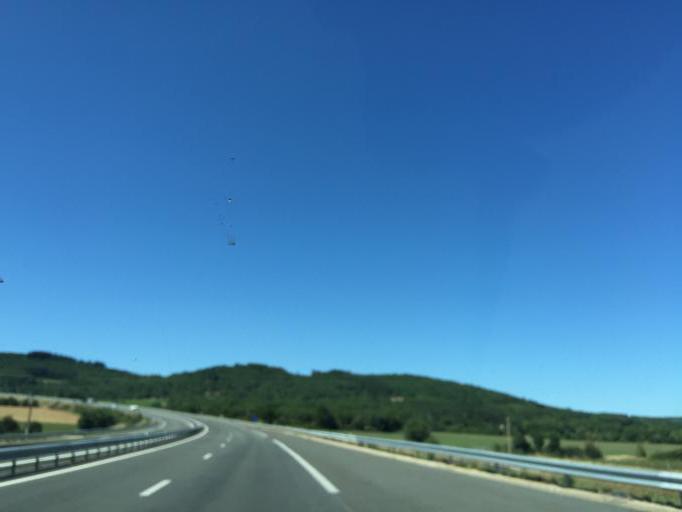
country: FR
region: Midi-Pyrenees
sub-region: Departement de l'Aveyron
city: La Cavalerie
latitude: 43.9667
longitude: 3.2099
